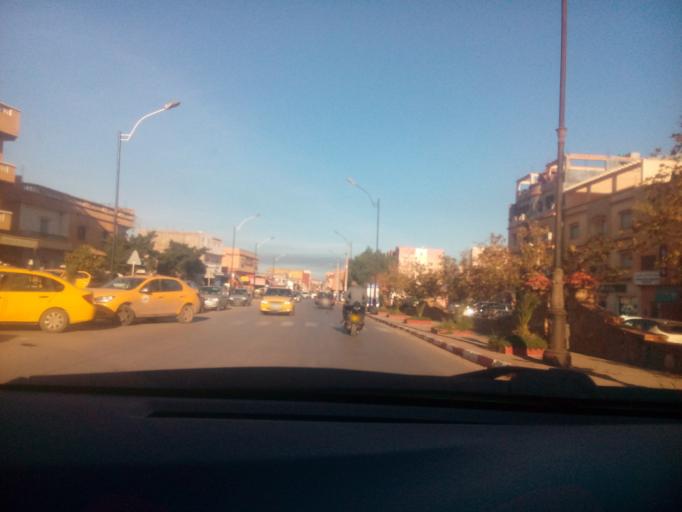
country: DZ
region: Oran
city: Bir el Djir
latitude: 35.7772
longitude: -0.4321
